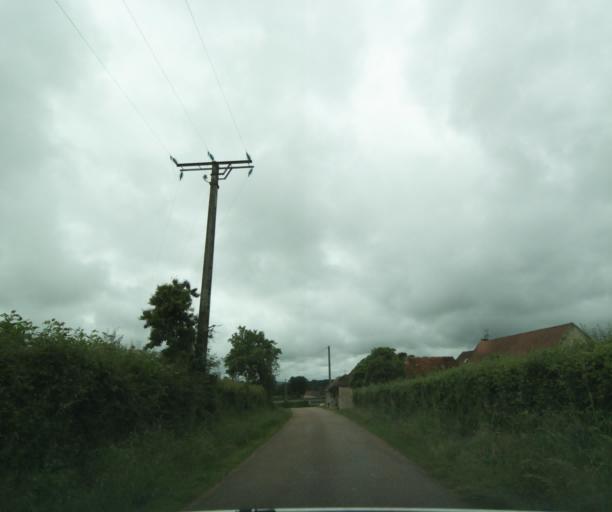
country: FR
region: Bourgogne
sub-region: Departement de Saone-et-Loire
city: Charolles
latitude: 46.4643
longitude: 4.3764
